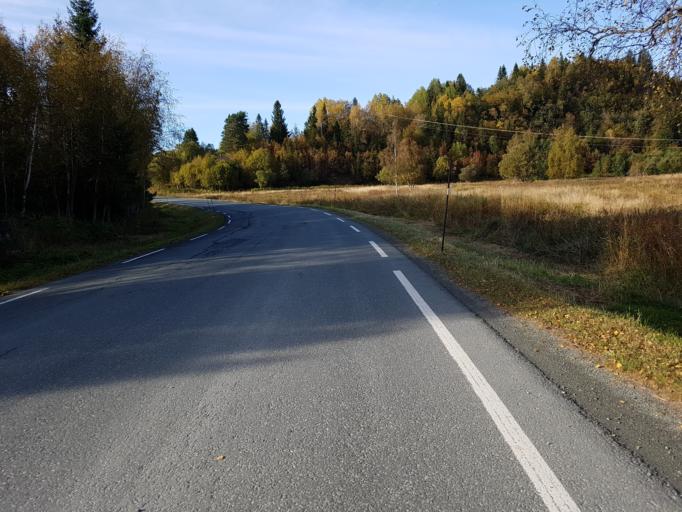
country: NO
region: Sor-Trondelag
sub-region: Klaebu
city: Klaebu
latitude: 63.3466
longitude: 10.5138
